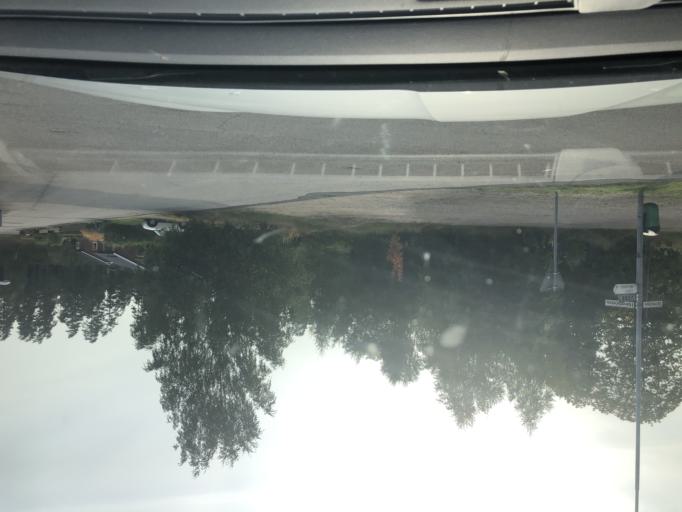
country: SE
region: Joenkoeping
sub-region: Vetlanda Kommun
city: Ekenassjon
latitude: 57.5181
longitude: 14.9051
